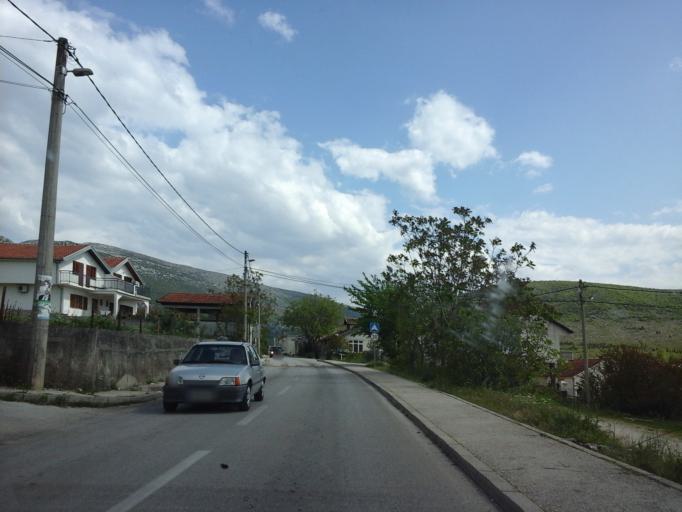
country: BA
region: Federation of Bosnia and Herzegovina
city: Blagaj
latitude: 43.2599
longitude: 17.8862
